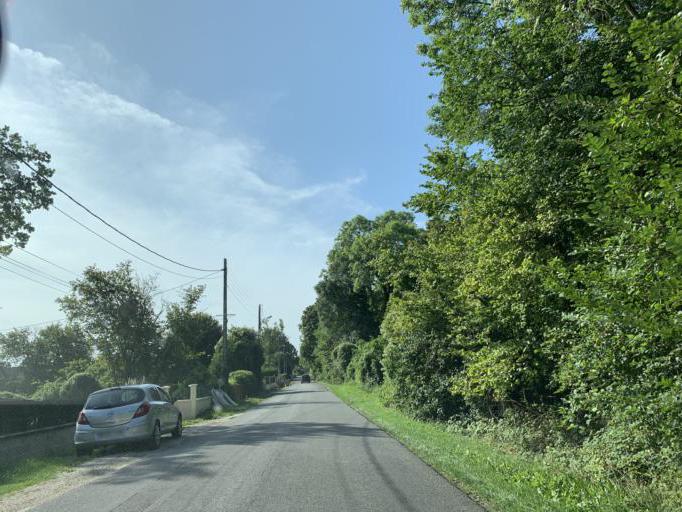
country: FR
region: Ile-de-France
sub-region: Departement de Seine-et-Marne
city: Chalifert
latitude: 48.9065
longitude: 2.7702
